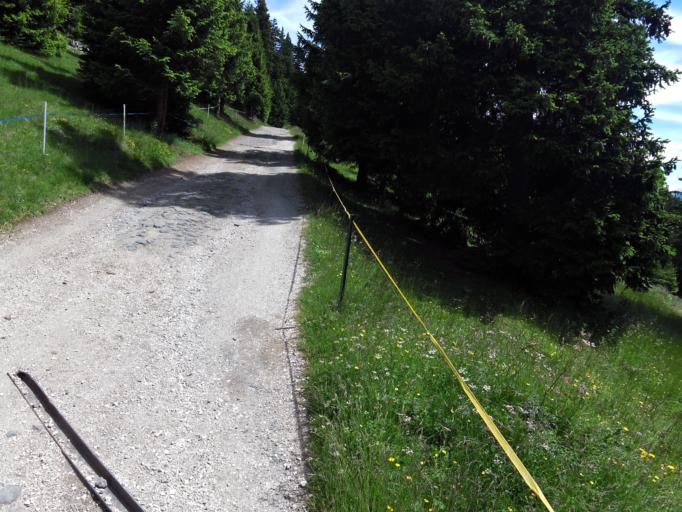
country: IT
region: Trentino-Alto Adige
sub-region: Bolzano
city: Ortisei
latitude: 46.5561
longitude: 11.6645
